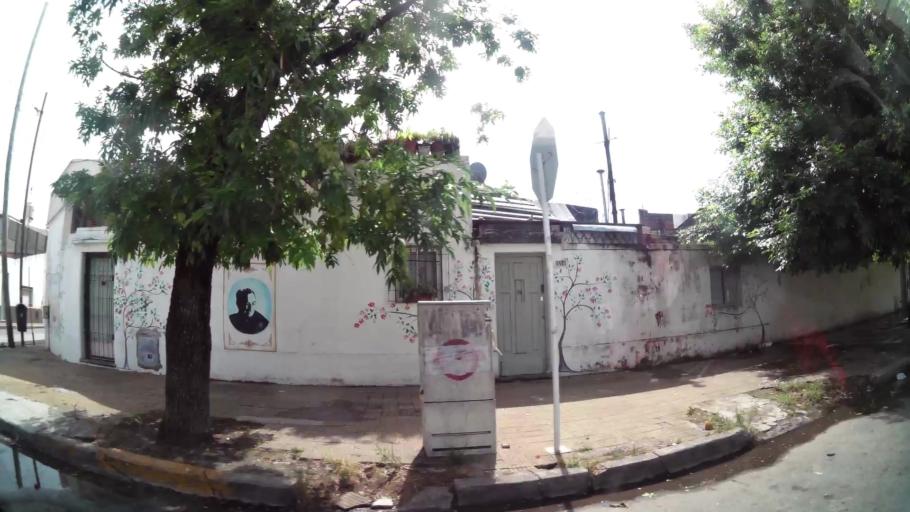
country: AR
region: Buenos Aires
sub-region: Partido de Avellaneda
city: Avellaneda
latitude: -34.6532
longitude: -58.4179
